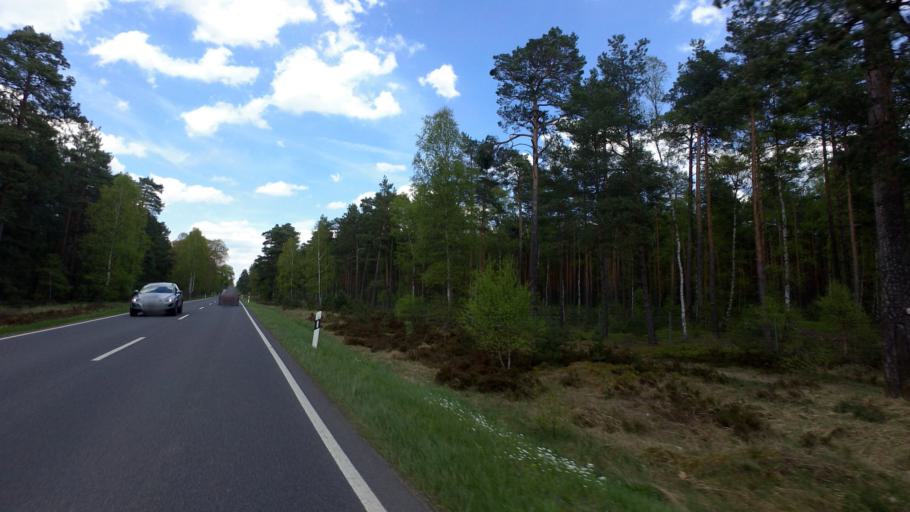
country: DE
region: Brandenburg
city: Marienwerder
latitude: 52.9612
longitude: 13.5698
